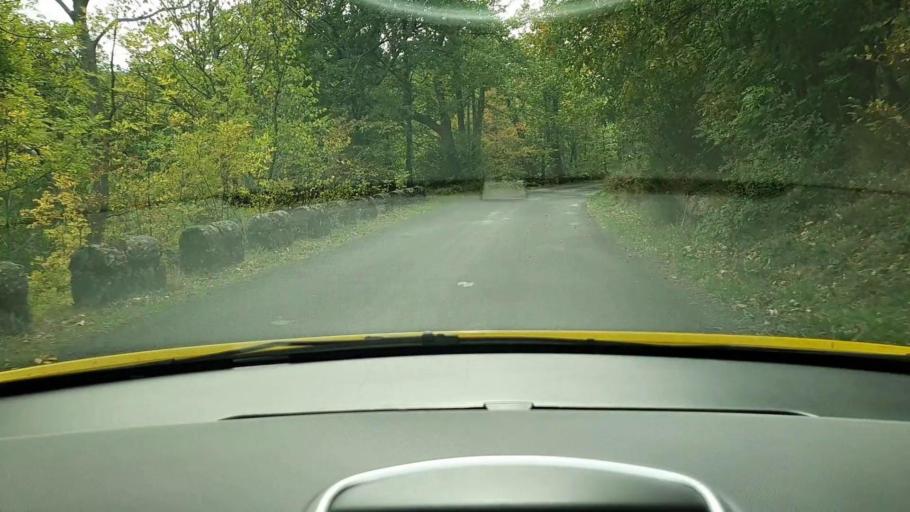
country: FR
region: Languedoc-Roussillon
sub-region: Departement de la Lozere
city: Meyrueis
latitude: 44.0701
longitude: 3.4496
